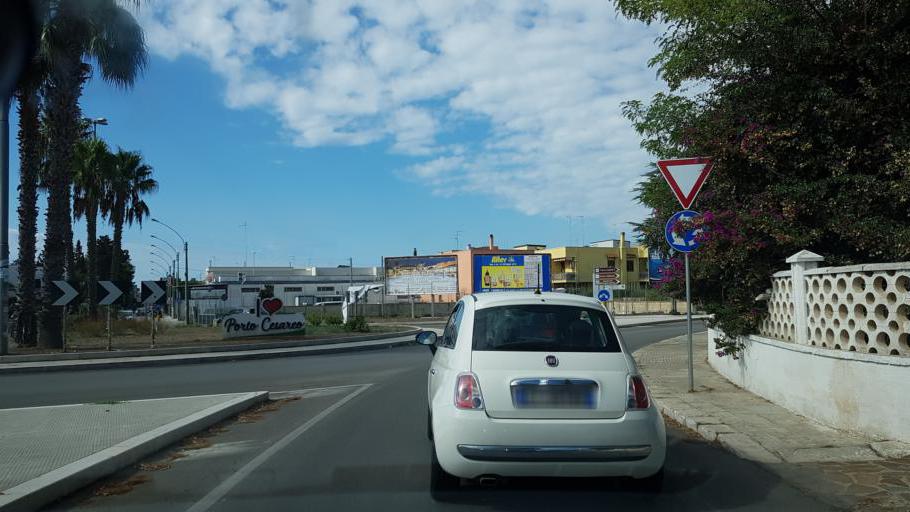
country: IT
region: Apulia
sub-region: Provincia di Lecce
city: Porto Cesareo
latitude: 40.2636
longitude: 17.9015
